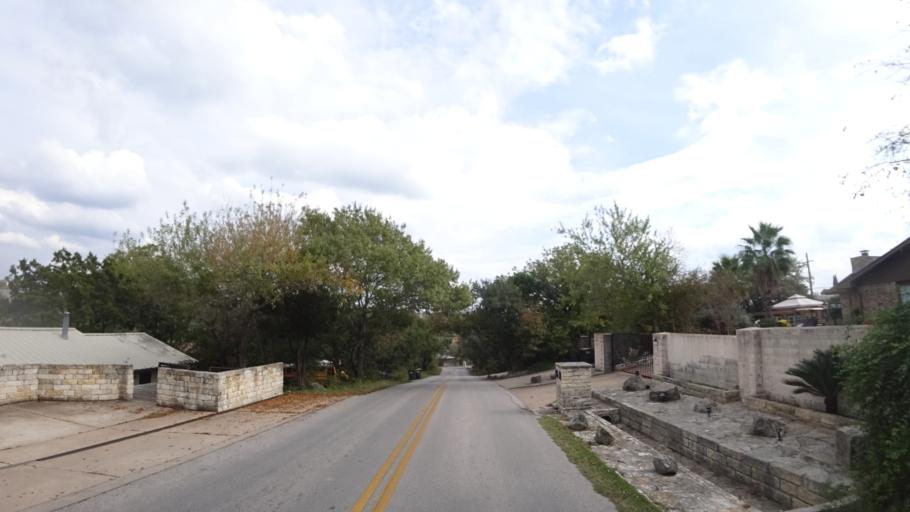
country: US
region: Texas
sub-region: Travis County
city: Hudson Bend
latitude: 30.3848
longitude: -97.9237
